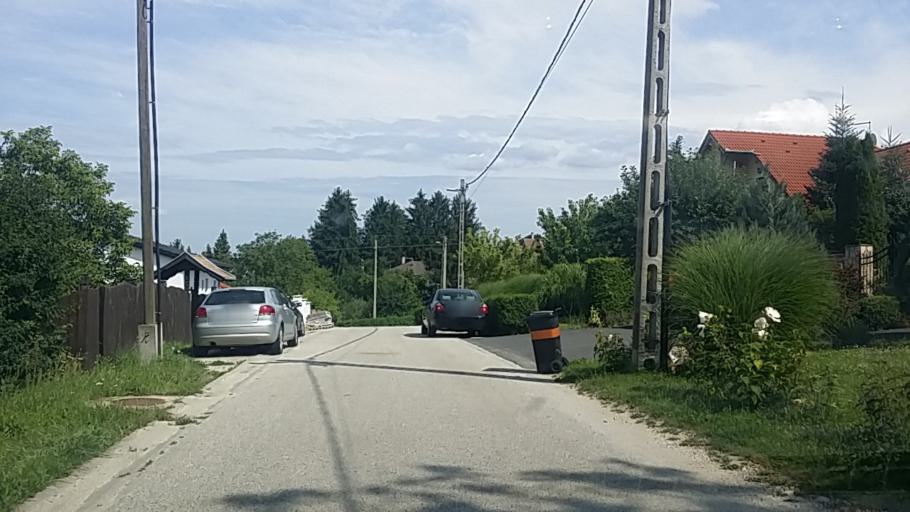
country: HU
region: Zala
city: Nagykanizsa
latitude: 46.4657
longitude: 17.0294
